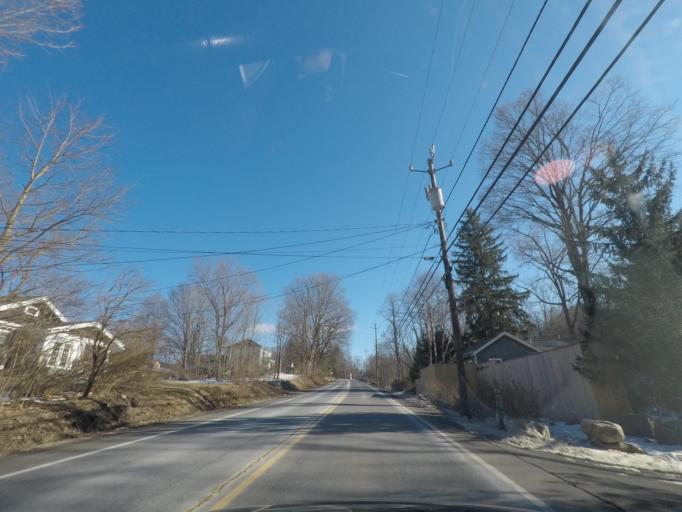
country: US
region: New York
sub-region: Columbia County
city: Chatham
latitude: 42.3286
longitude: -73.5507
